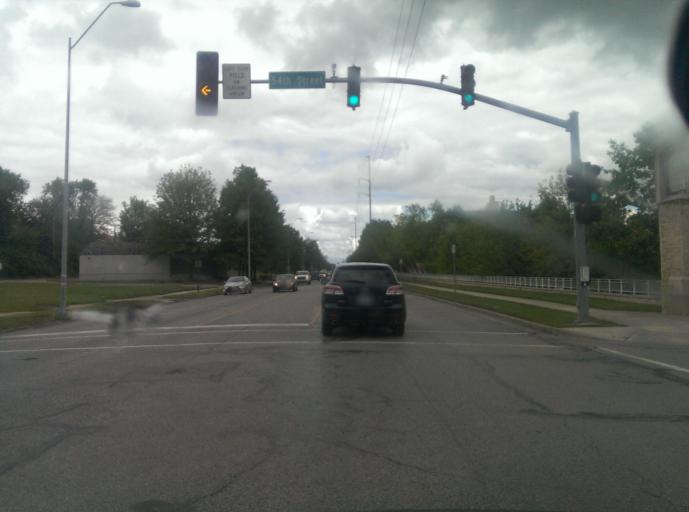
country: US
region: Kansas
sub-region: Johnson County
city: Mission Hills
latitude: 39.0288
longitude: -94.5737
